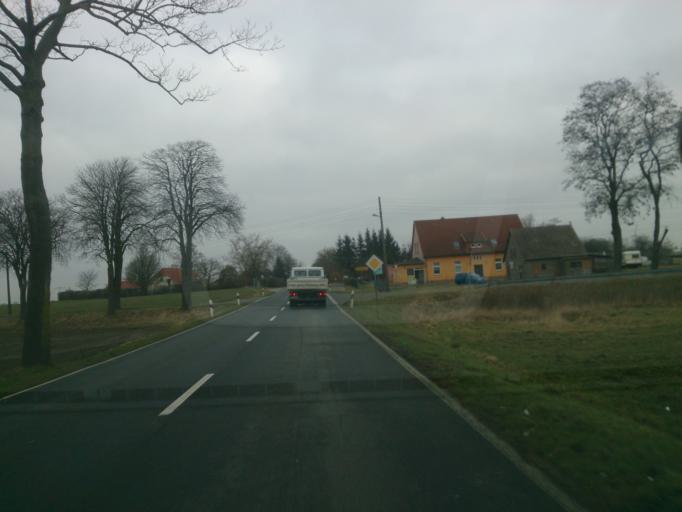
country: DE
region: Mecklenburg-Vorpommern
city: Borrentin
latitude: 53.8237
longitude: 12.9802
